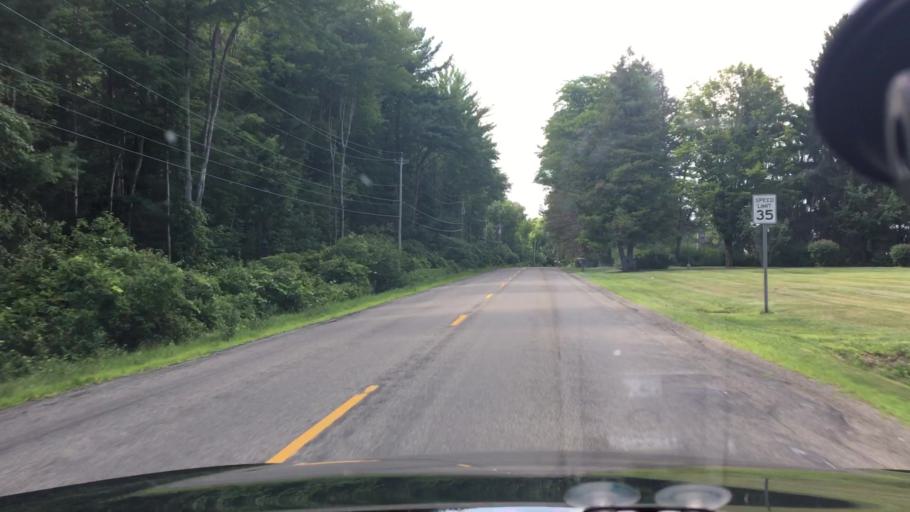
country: US
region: New York
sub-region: Chautauqua County
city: Lakewood
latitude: 42.1041
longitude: -79.3809
